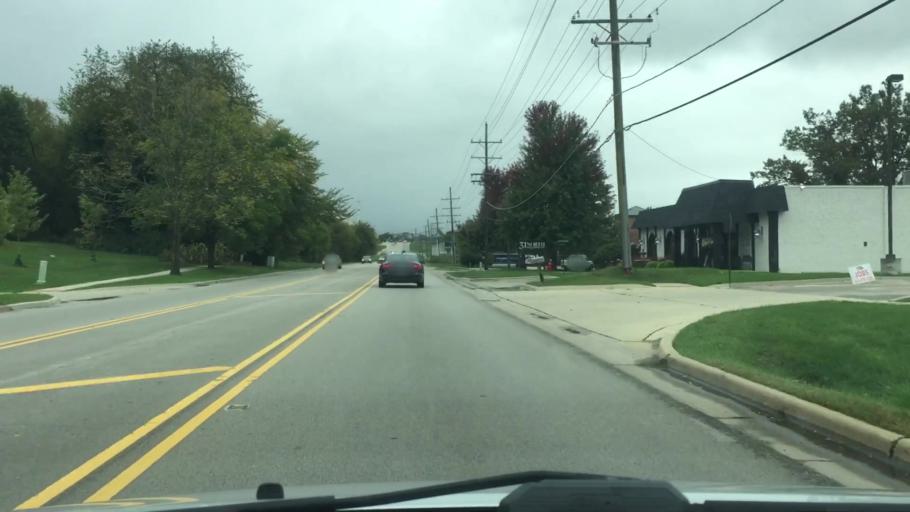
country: US
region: Illinois
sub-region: McHenry County
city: McHenry
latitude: 42.3316
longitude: -88.2745
